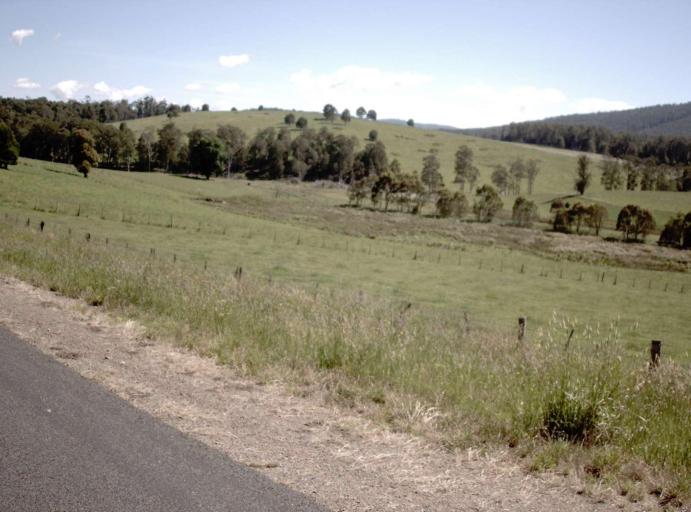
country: AU
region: New South Wales
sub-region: Bombala
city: Bombala
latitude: -37.1743
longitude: 148.7239
